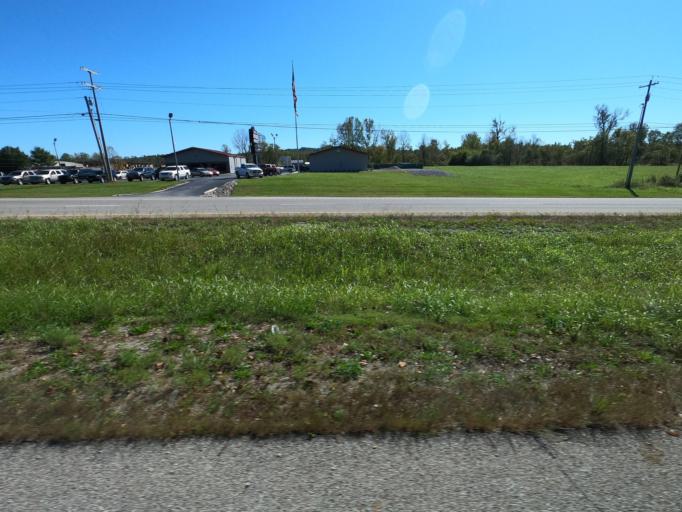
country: US
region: Tennessee
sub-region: Maury County
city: Mount Pleasant
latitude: 35.5075
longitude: -87.2274
